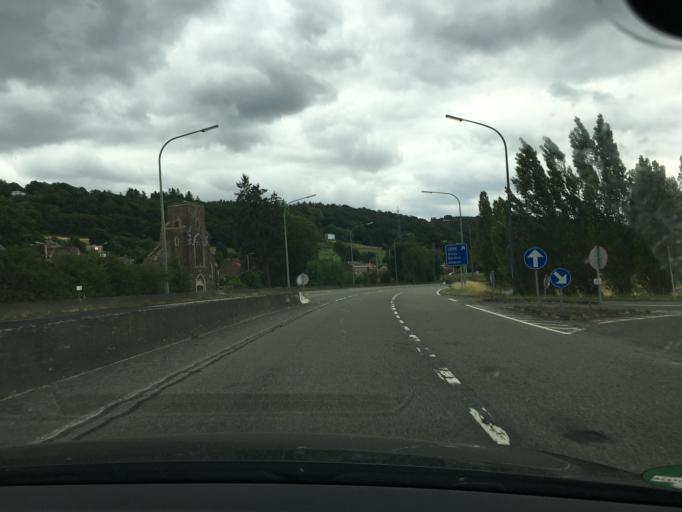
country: BE
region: Wallonia
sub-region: Province de Liege
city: Amay
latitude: 50.5457
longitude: 5.3363
